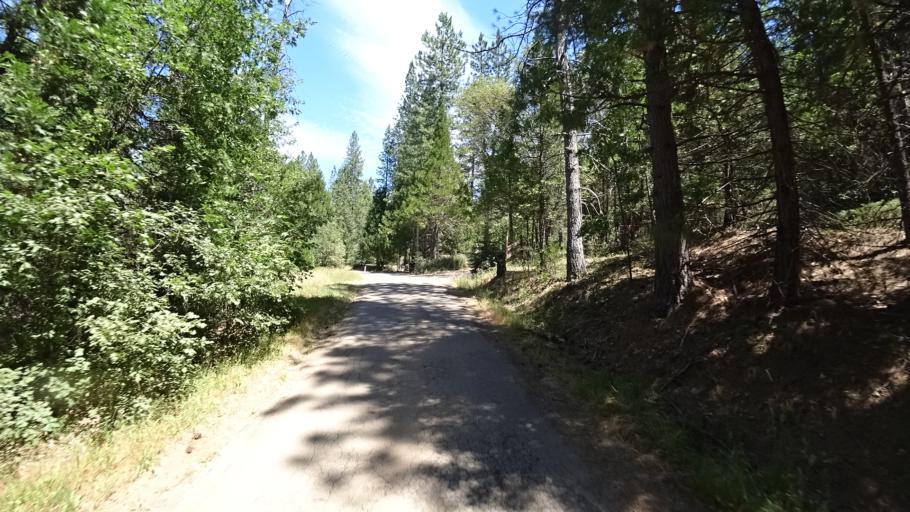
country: US
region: California
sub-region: Calaveras County
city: Arnold
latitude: 38.2569
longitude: -120.4196
